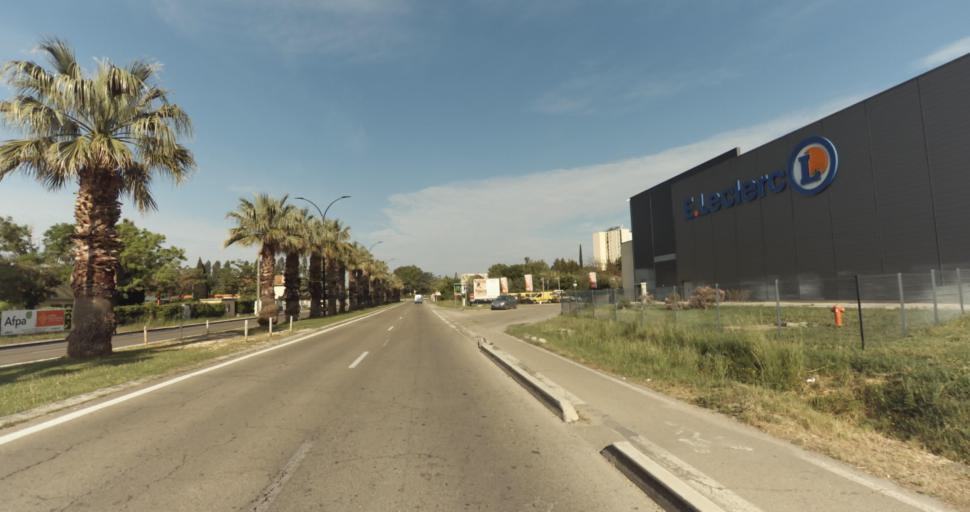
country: FR
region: Languedoc-Roussillon
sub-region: Departement du Gard
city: Rodilhan
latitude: 43.8367
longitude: 4.3915
